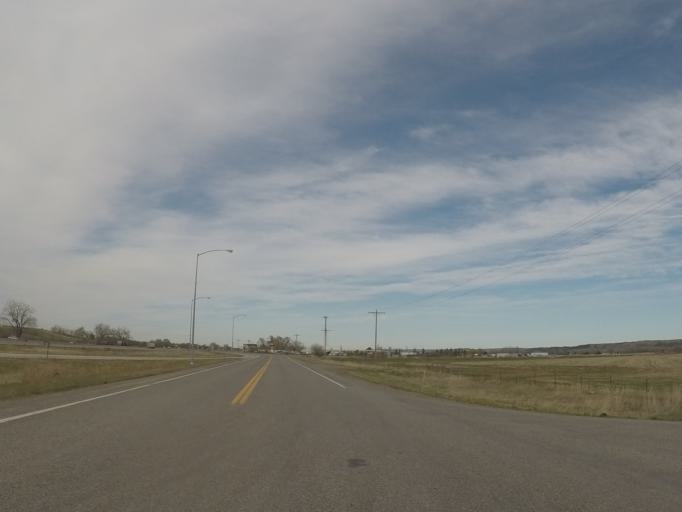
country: US
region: Montana
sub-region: Yellowstone County
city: Laurel
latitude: 45.6940
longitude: -108.6796
